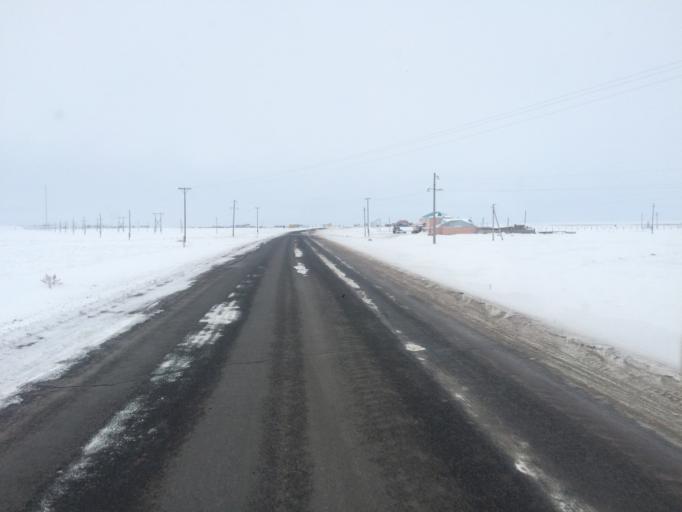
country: RU
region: Orenburg
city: Dombarovskiy
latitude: 49.9581
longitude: 60.0825
